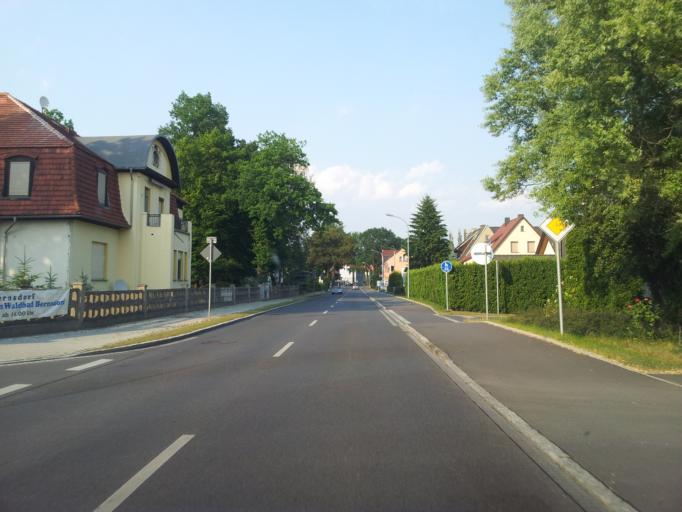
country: DE
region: Saxony
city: Bernsdorf
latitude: 51.3612
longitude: 14.0456
